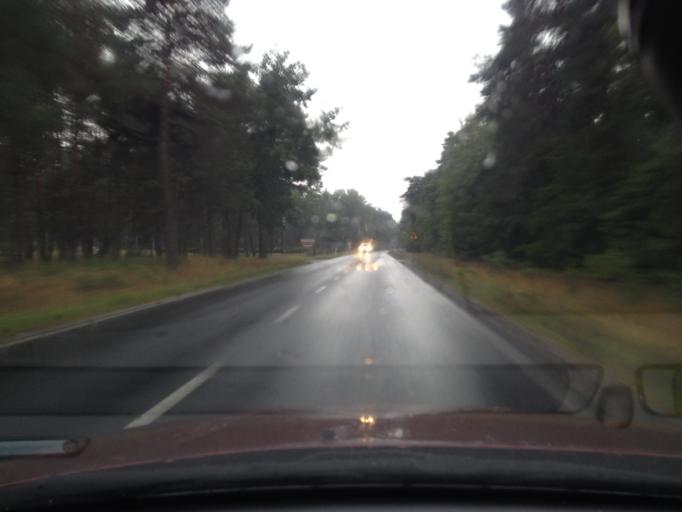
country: PL
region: Lubusz
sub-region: Powiat zaganski
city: Zagan
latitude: 51.5986
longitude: 15.2921
